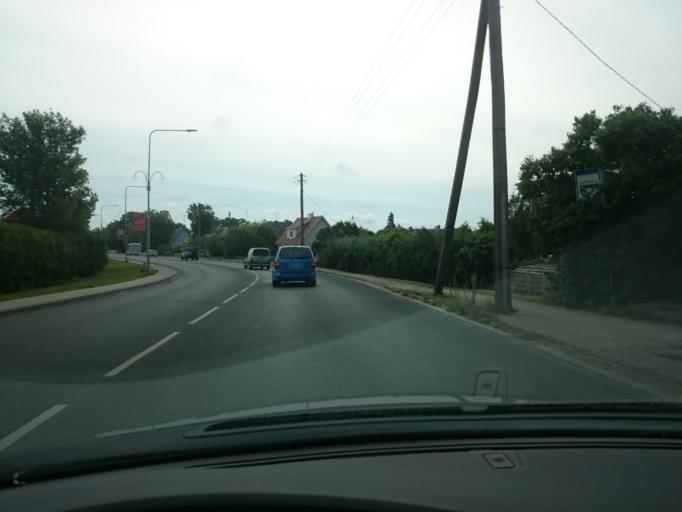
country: EE
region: Laeaene
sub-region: Haapsalu linn
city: Haapsalu
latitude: 58.9388
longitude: 23.5461
